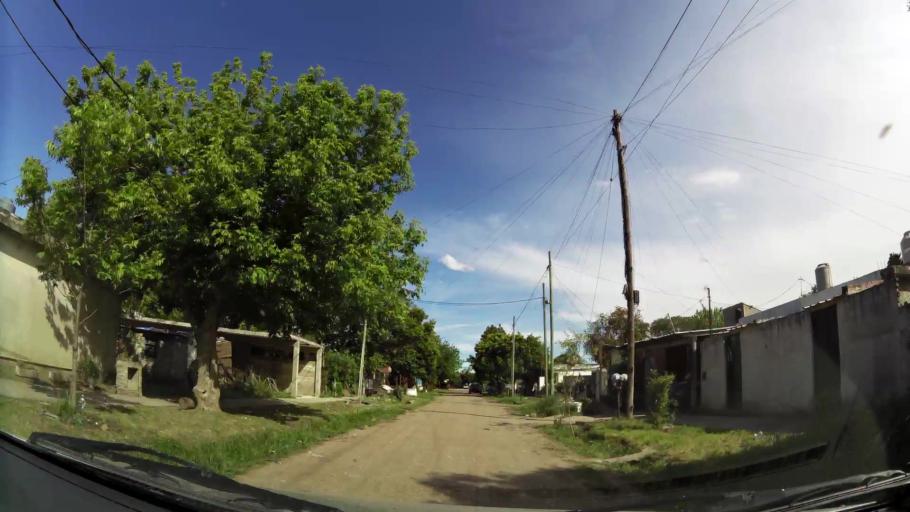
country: AR
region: Buenos Aires
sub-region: Partido de Almirante Brown
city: Adrogue
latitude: -34.8036
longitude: -58.3589
